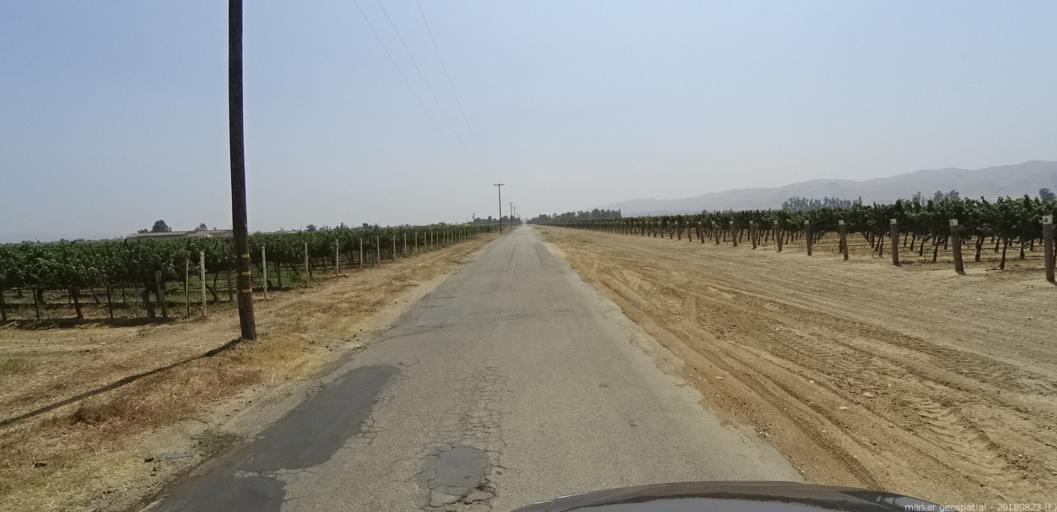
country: US
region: California
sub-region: Monterey County
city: Greenfield
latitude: 36.3240
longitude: -121.2679
